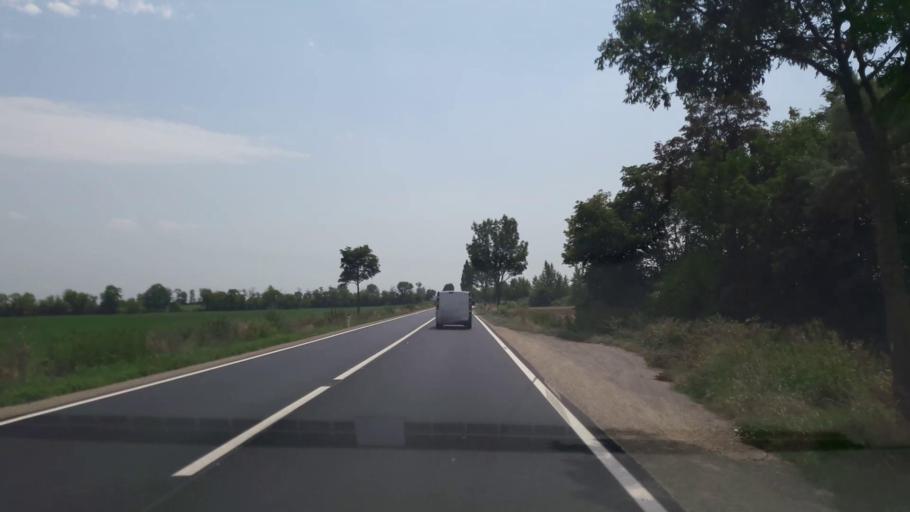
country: AT
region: Lower Austria
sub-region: Politischer Bezirk Wien-Umgebung
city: Schwechat
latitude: 48.1319
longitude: 16.4976
